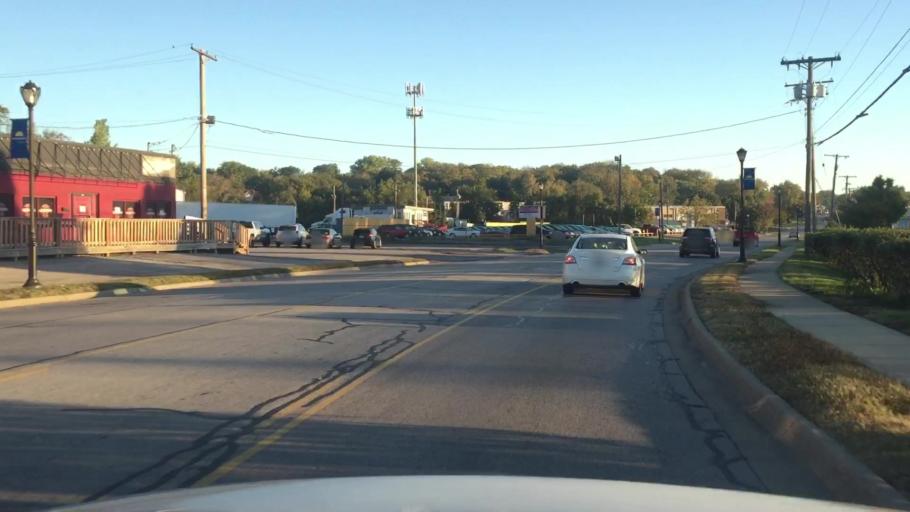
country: US
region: Kansas
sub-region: Johnson County
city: Merriam
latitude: 39.0332
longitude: -94.6911
